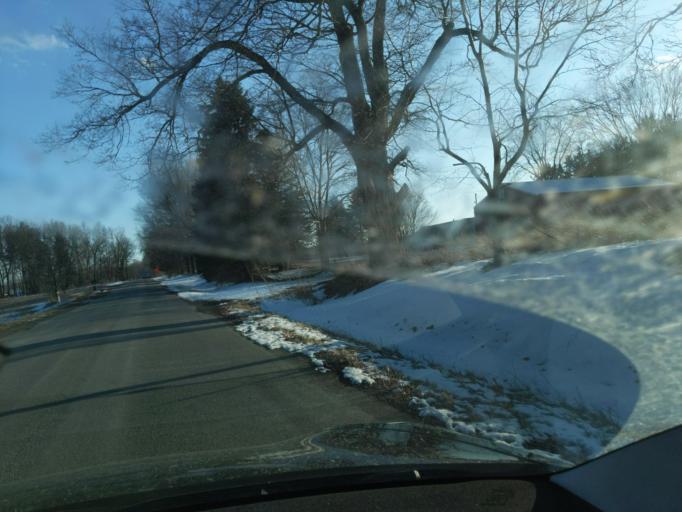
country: US
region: Michigan
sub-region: Ingham County
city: Stockbridge
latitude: 42.5164
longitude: -84.2444
